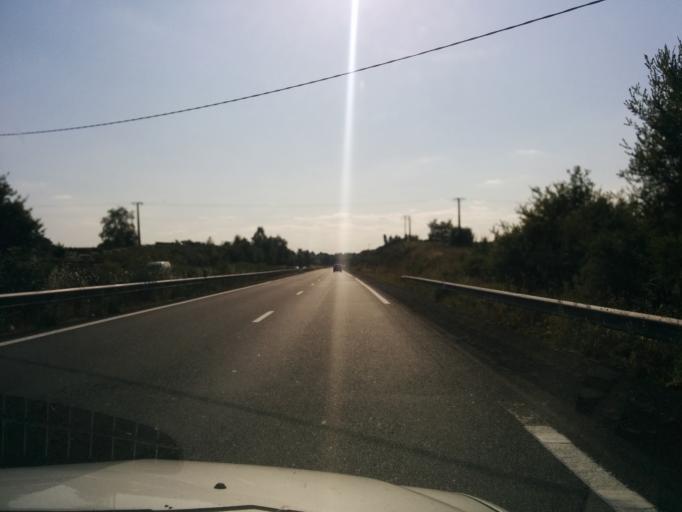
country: FR
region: Pays de la Loire
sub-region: Departement de la Loire-Atlantique
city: Vallet
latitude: 47.1556
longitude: -1.2522
